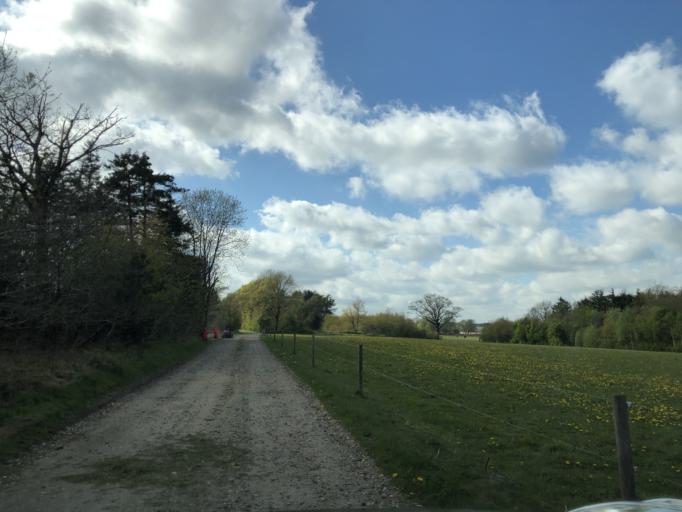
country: DK
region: Central Jutland
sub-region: Herning Kommune
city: Avlum
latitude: 56.2962
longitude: 8.7546
